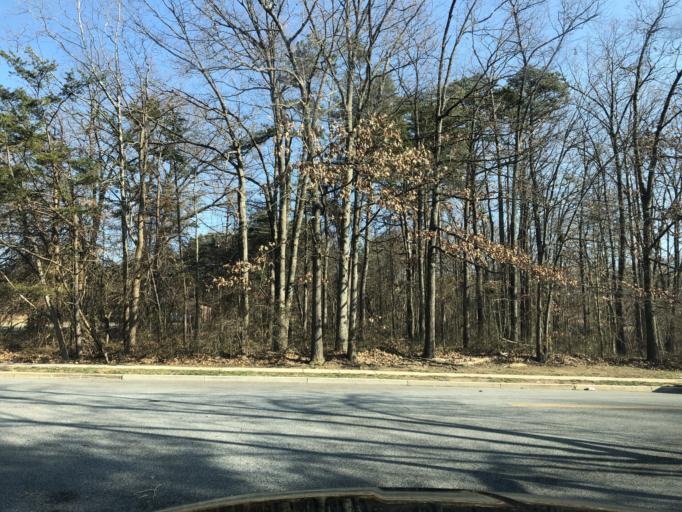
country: US
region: Maryland
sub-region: Anne Arundel County
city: Odenton
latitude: 39.0849
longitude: -76.6874
